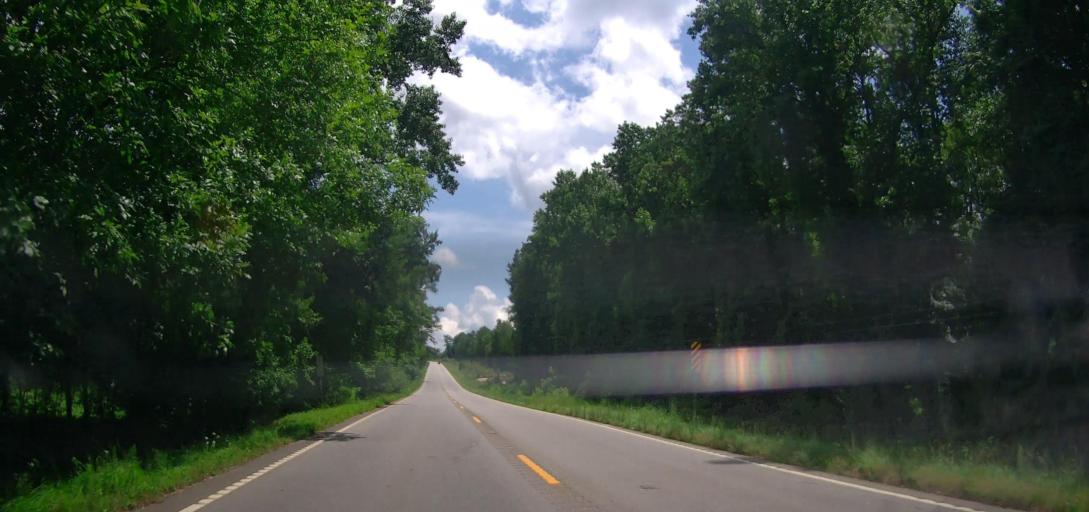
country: US
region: Georgia
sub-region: Meriwether County
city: Greenville
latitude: 33.0034
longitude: -84.6426
